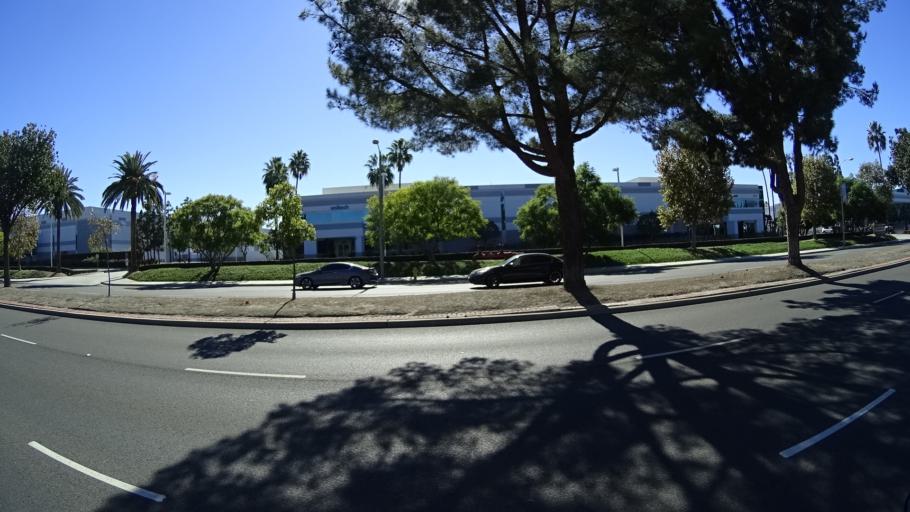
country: US
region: California
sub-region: Orange County
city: Cypress
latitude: 33.8031
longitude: -118.0259
